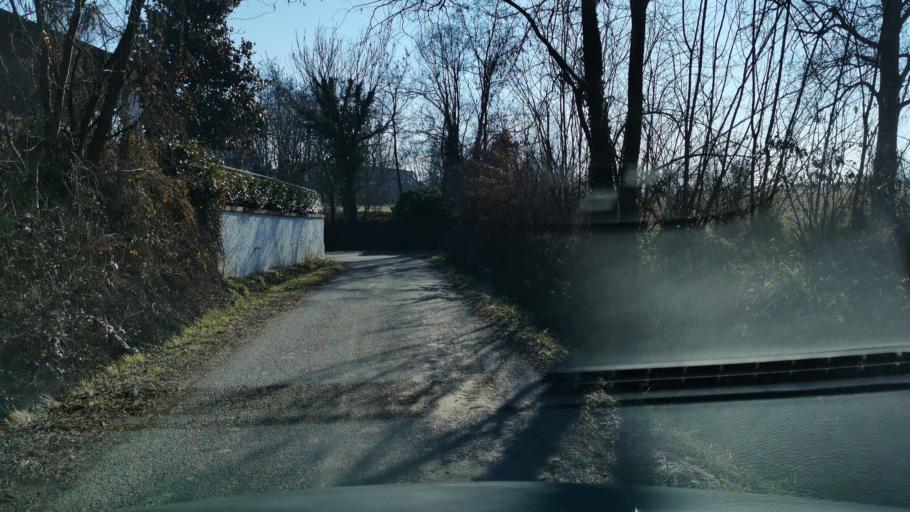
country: IT
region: Piedmont
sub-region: Provincia di Torino
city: Leini
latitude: 45.2118
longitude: 7.7075
